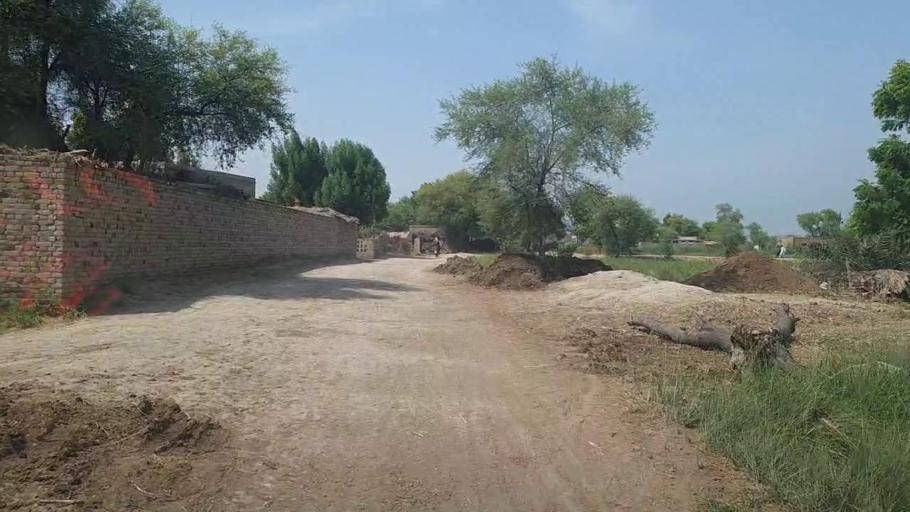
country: PK
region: Sindh
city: Ubauro
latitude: 28.1791
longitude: 69.8148
